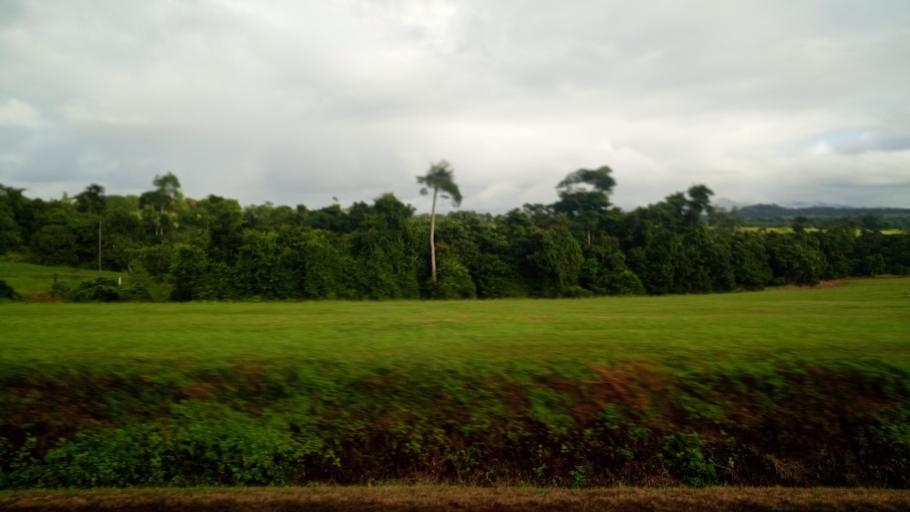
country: AU
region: Queensland
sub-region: Cassowary Coast
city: Innisfail
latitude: -17.5481
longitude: 145.9649
